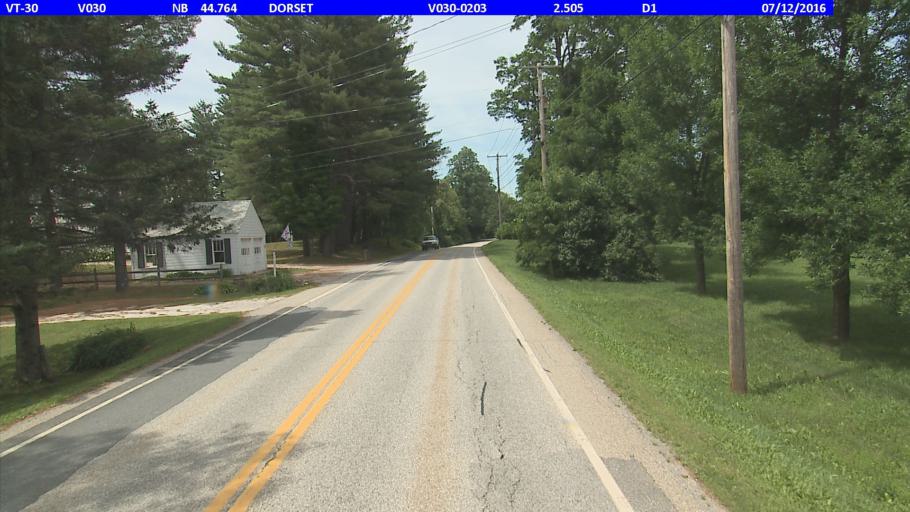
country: US
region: Vermont
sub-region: Bennington County
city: Manchester Center
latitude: 43.2441
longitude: -73.0905
